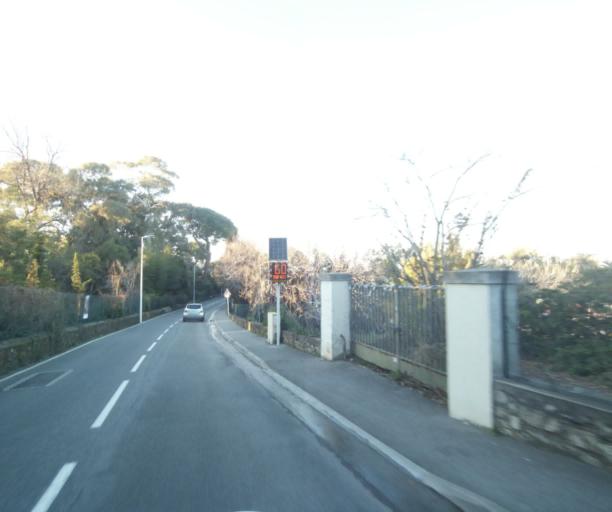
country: FR
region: Provence-Alpes-Cote d'Azur
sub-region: Departement des Alpes-Maritimes
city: Antibes
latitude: 43.5643
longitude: 7.1253
